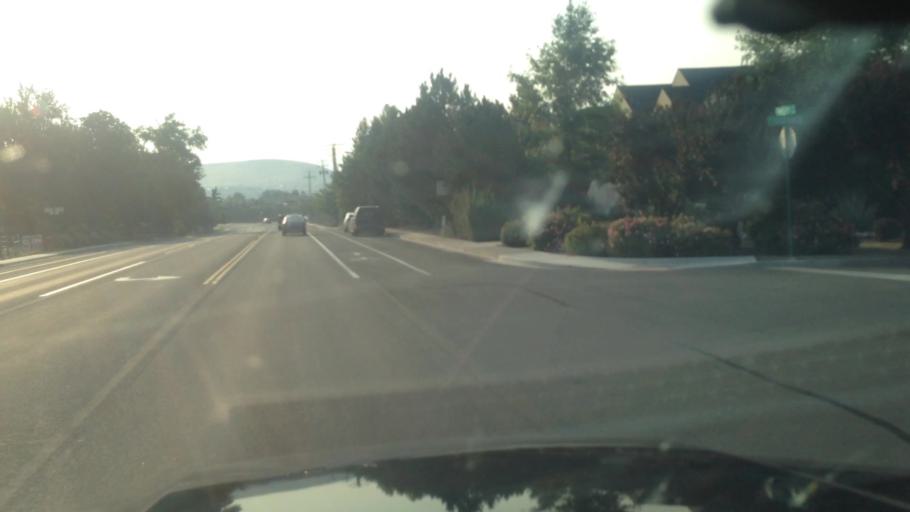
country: US
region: Nevada
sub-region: Washoe County
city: Reno
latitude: 39.5064
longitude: -119.8554
